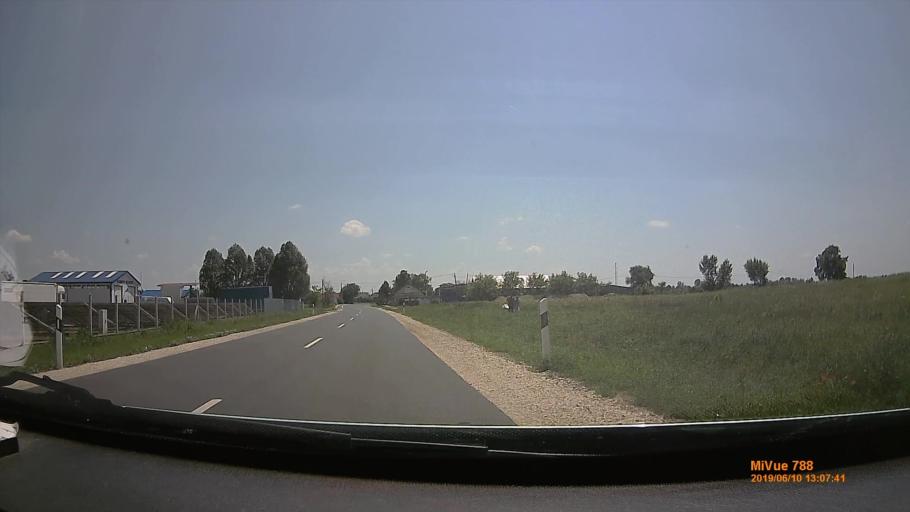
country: HU
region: Borsod-Abauj-Zemplen
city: Gesztely
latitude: 48.0854
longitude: 20.9695
